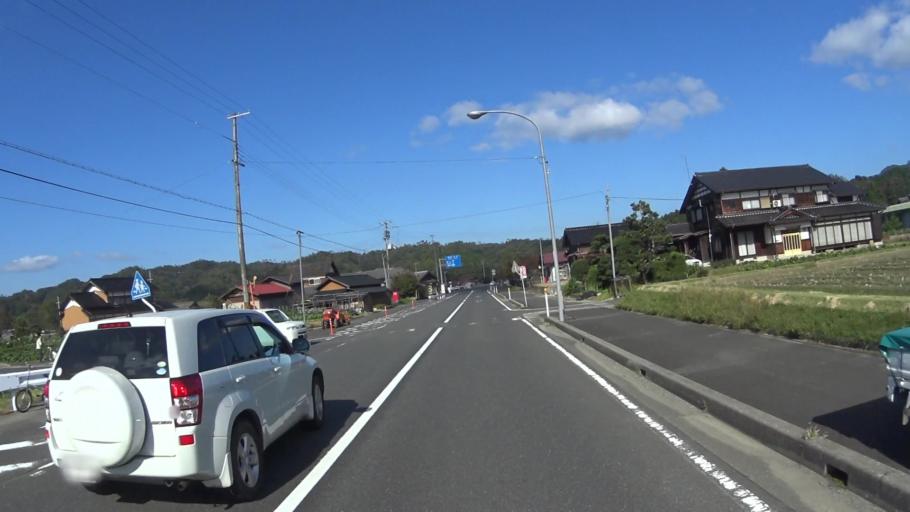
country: JP
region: Kyoto
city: Miyazu
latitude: 35.5959
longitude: 135.1425
